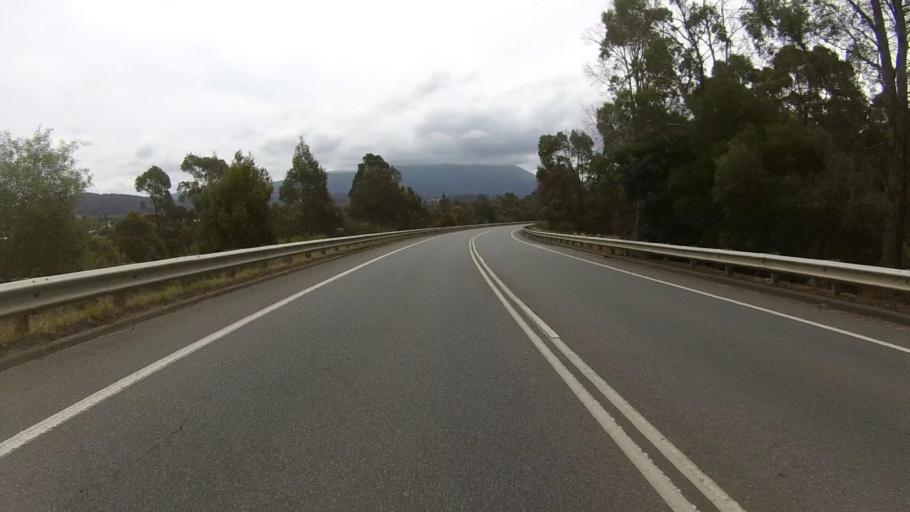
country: AU
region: Tasmania
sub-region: Kingborough
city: Kingston
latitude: -42.9949
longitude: 147.2954
